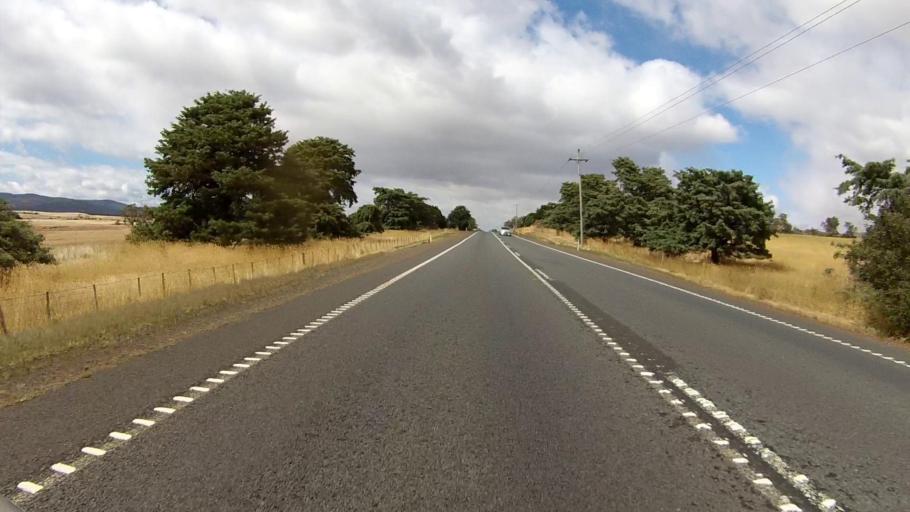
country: AU
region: Tasmania
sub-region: Northern Midlands
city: Evandale
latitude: -41.9517
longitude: 147.4952
